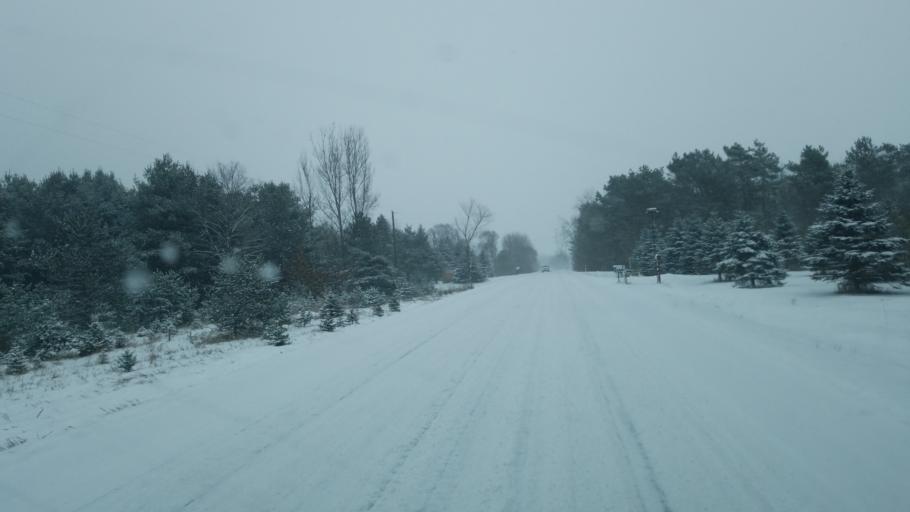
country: US
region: Michigan
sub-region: Mecosta County
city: Canadian Lakes
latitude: 43.5766
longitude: -85.3873
